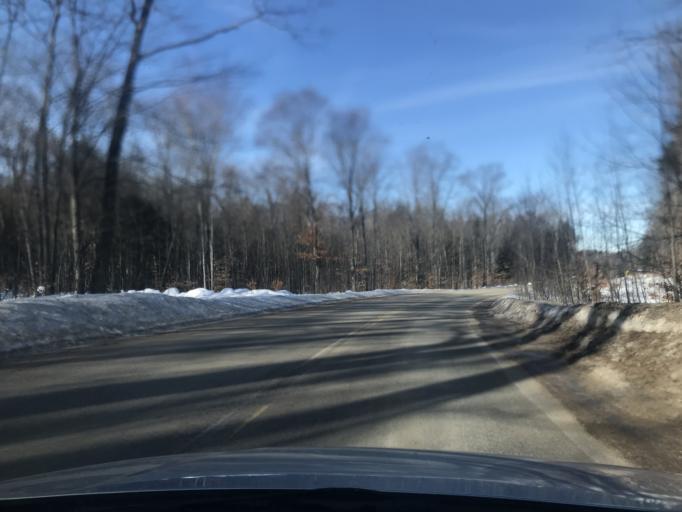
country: US
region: Michigan
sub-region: Dickinson County
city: Kingsford
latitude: 45.4081
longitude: -88.3509
